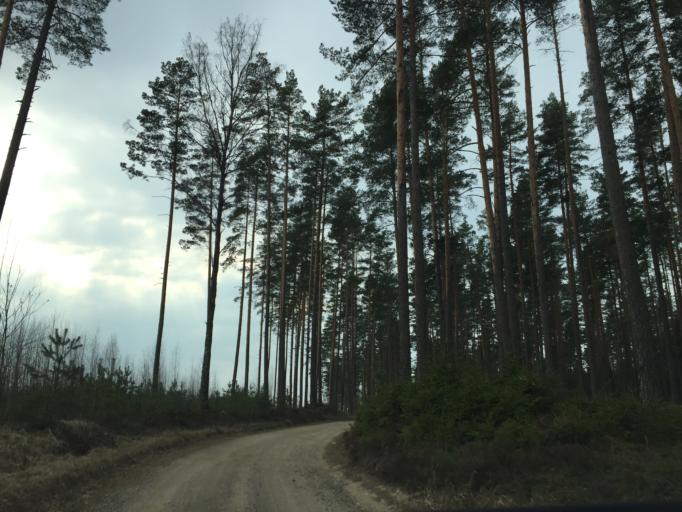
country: LV
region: Amatas Novads
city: Drabesi
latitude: 57.2084
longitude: 25.2461
